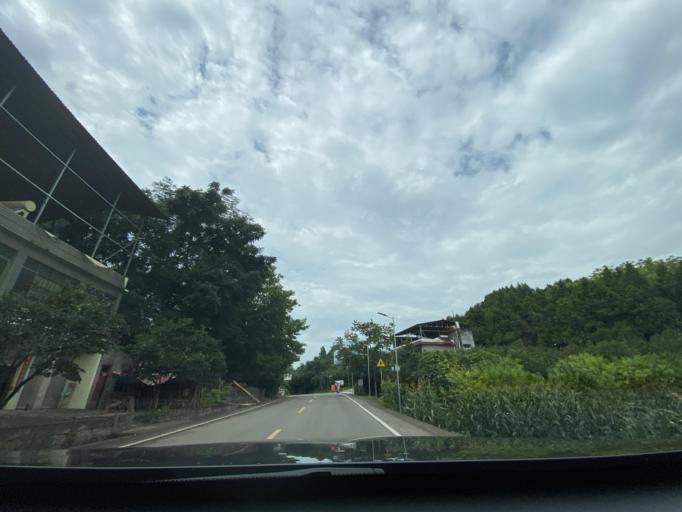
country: CN
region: Sichuan
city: Jiancheng
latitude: 30.4815
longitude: 104.6334
